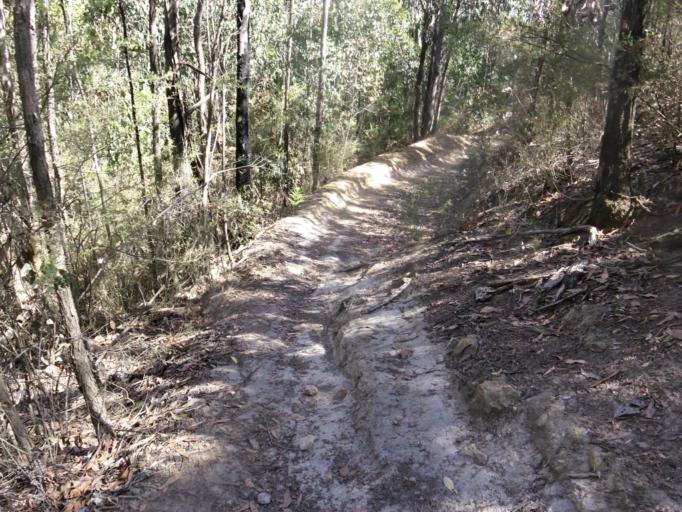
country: AU
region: Victoria
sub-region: Nillumbik
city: Saint Andrews
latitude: -37.5235
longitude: 145.3036
